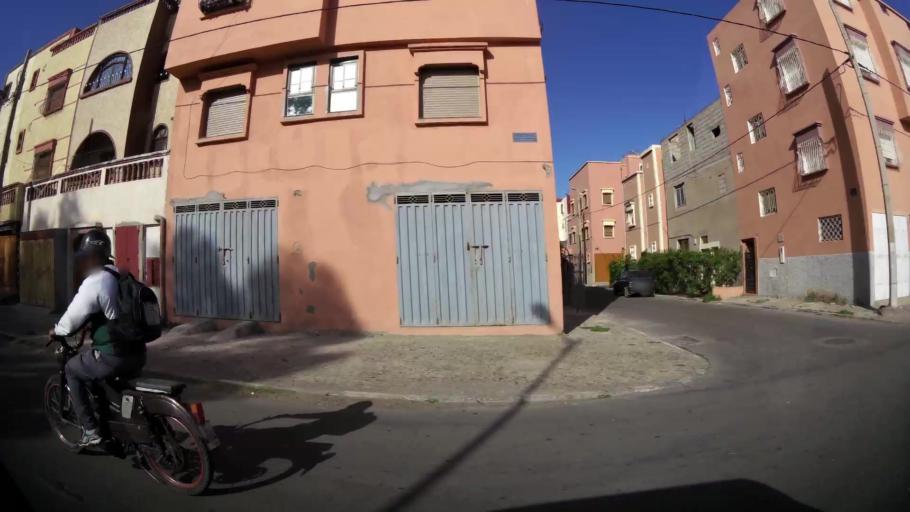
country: MA
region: Souss-Massa-Draa
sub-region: Inezgane-Ait Mellou
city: Inezgane
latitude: 30.3655
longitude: -9.5278
